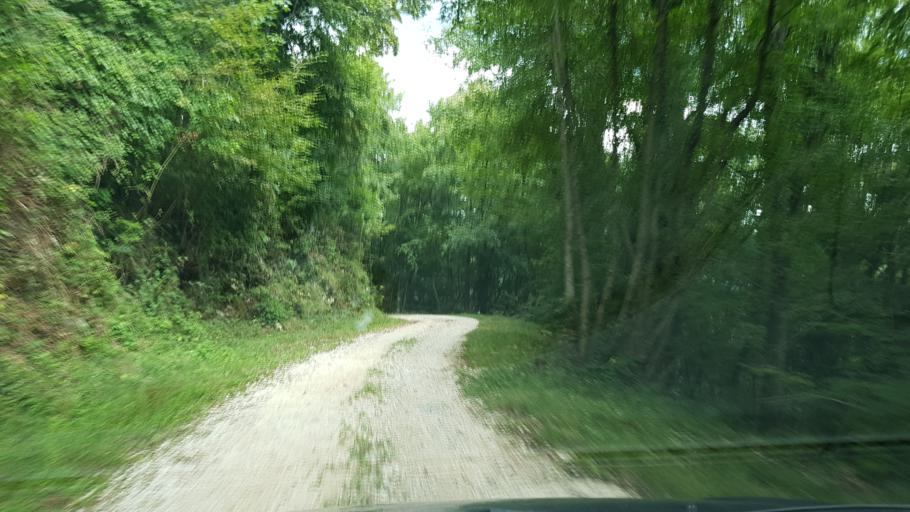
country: SI
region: Kanal
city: Deskle
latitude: 46.0583
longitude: 13.5734
